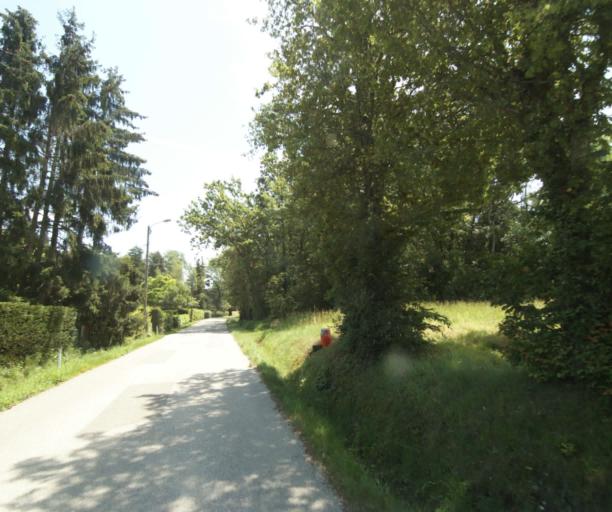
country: FR
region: Rhone-Alpes
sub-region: Departement de la Haute-Savoie
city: Messery
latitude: 46.3638
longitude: 6.3090
